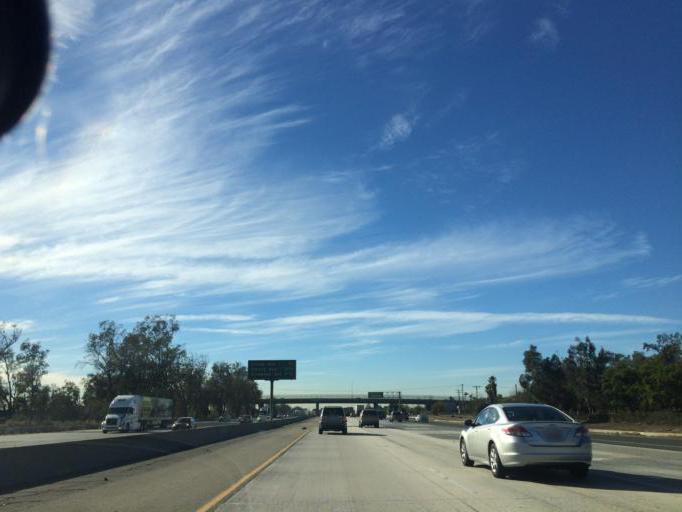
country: US
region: California
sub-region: San Bernardino County
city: Fontana
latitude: 34.0671
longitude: -117.4403
